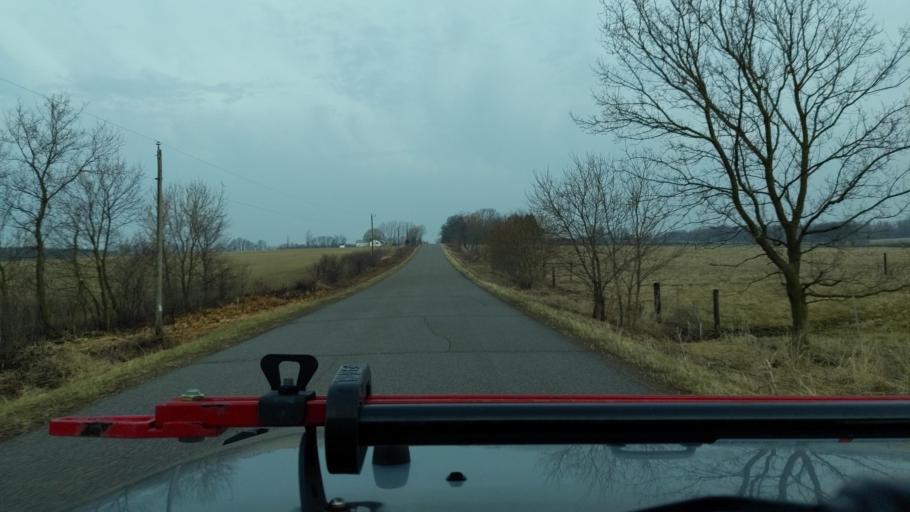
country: US
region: Wisconsin
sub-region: Saint Croix County
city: Baldwin
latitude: 44.9345
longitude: -92.4062
